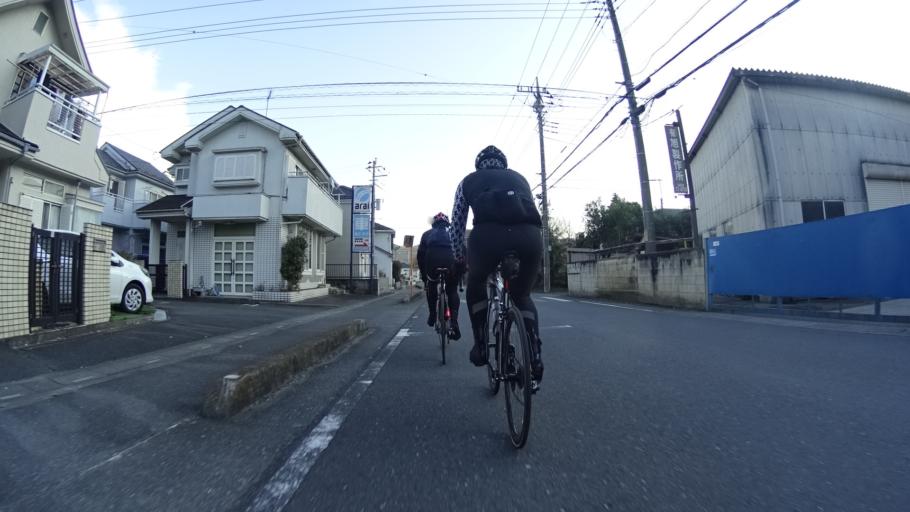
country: JP
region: Saitama
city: Hanno
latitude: 35.8427
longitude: 139.3176
